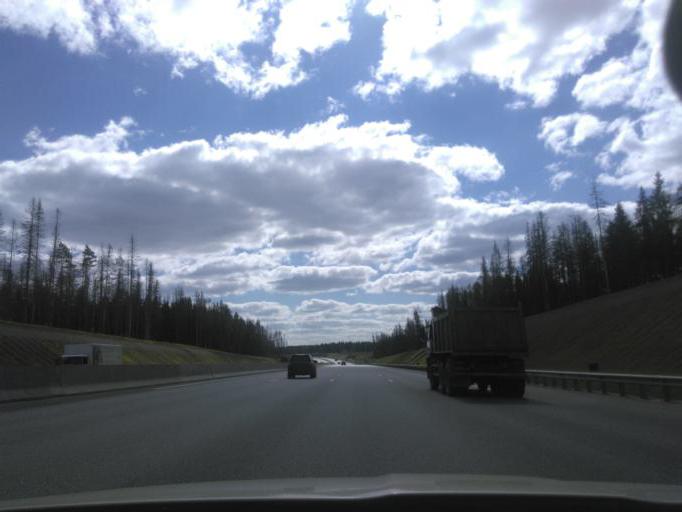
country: RU
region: Moskovskaya
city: Skhodnya
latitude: 55.9794
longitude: 37.3159
